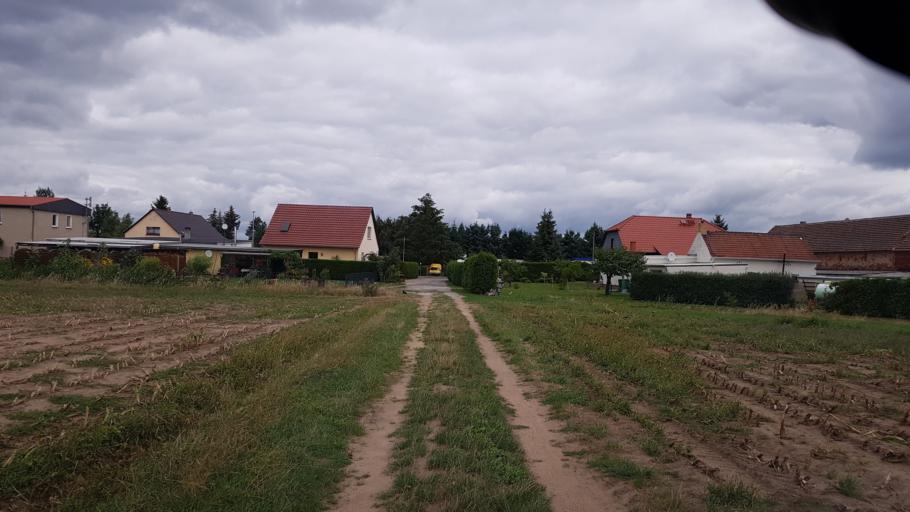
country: DE
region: Brandenburg
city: Bad Liebenwerda
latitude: 51.5470
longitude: 13.3303
